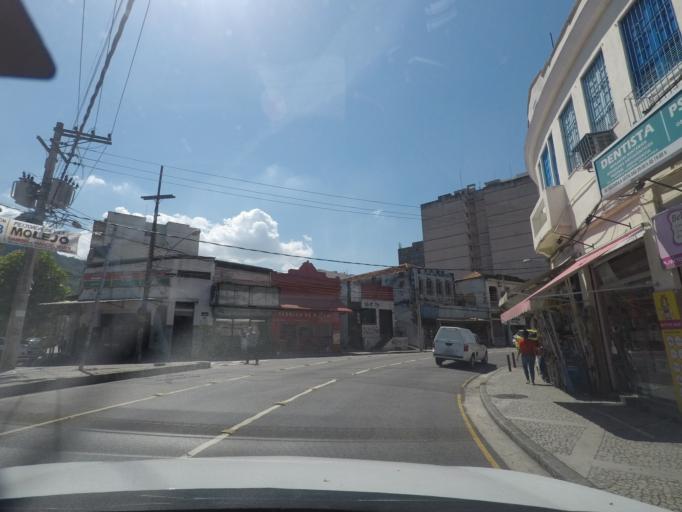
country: BR
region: Rio de Janeiro
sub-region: Rio De Janeiro
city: Rio de Janeiro
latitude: -22.9237
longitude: -43.2582
